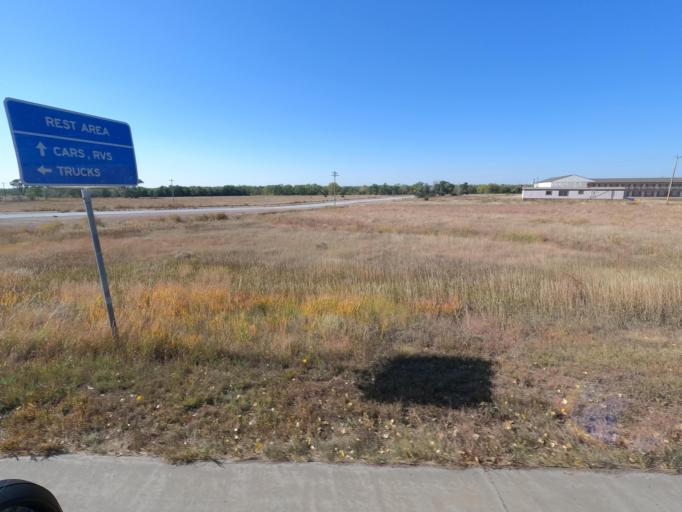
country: US
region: Colorado
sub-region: Sedgwick County
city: Julesburg
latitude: 40.9681
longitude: -102.2497
